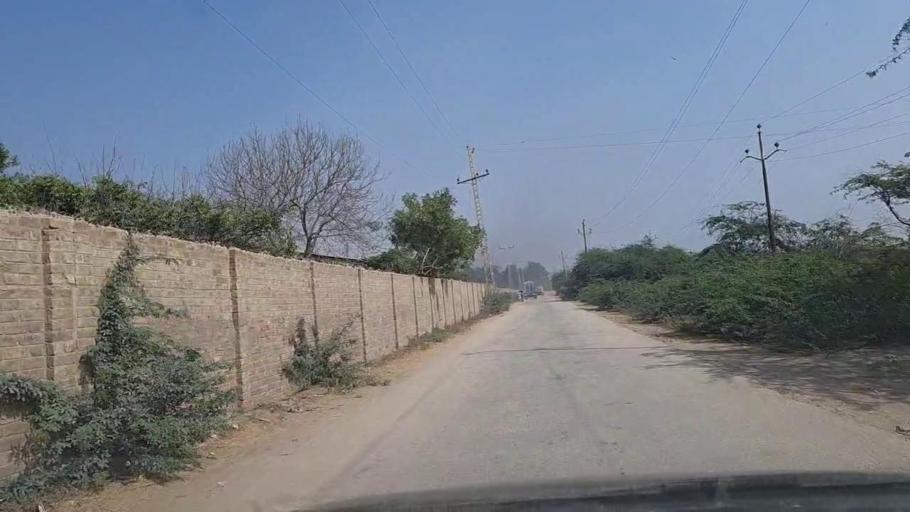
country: PK
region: Sindh
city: Gharo
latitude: 24.7374
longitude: 67.6001
